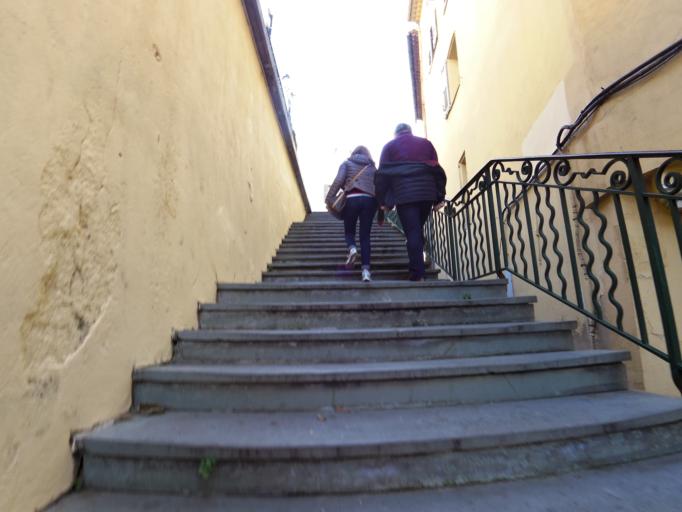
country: FR
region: Provence-Alpes-Cote d'Azur
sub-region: Departement des Alpes-Maritimes
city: Grasse
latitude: 43.6579
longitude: 6.9240
